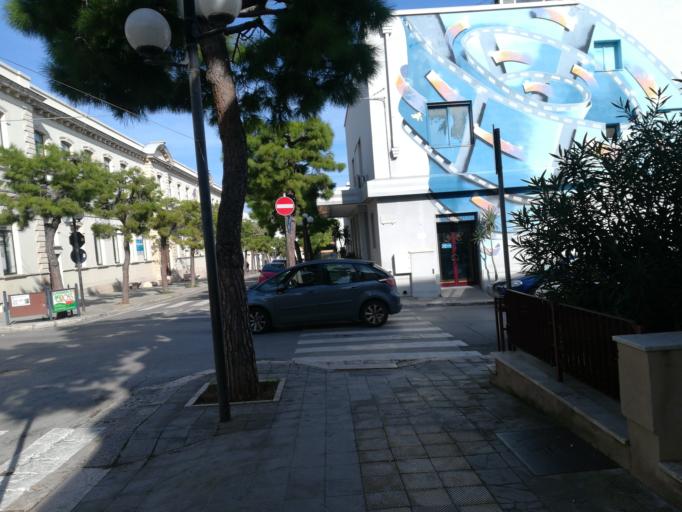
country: IT
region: Apulia
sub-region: Provincia di Bari
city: Polignano a Mare
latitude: 40.9919
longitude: 17.2193
